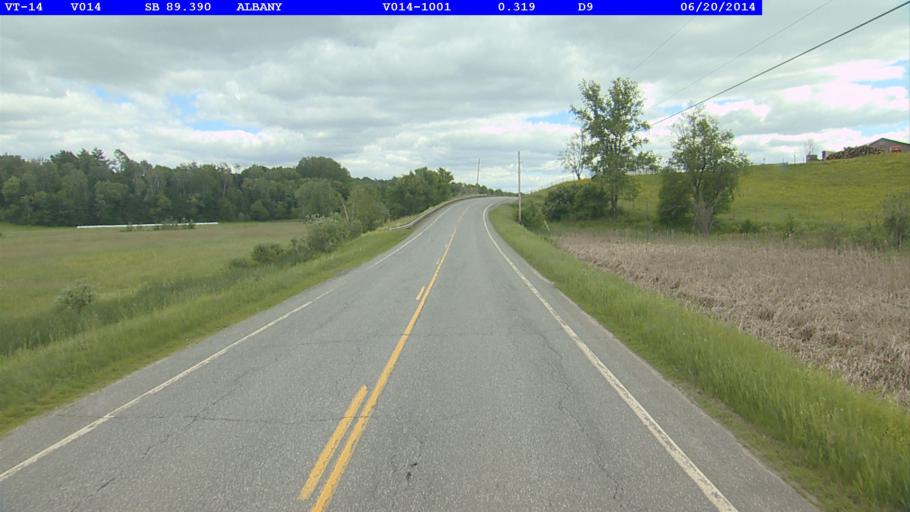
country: US
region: Vermont
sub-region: Caledonia County
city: Hardwick
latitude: 44.7071
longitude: -72.3897
